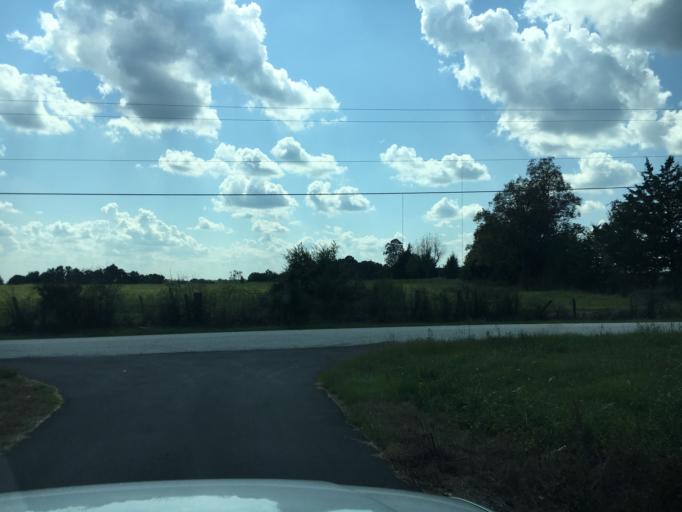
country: US
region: South Carolina
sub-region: Laurens County
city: Laurens
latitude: 34.5793
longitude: -82.0970
